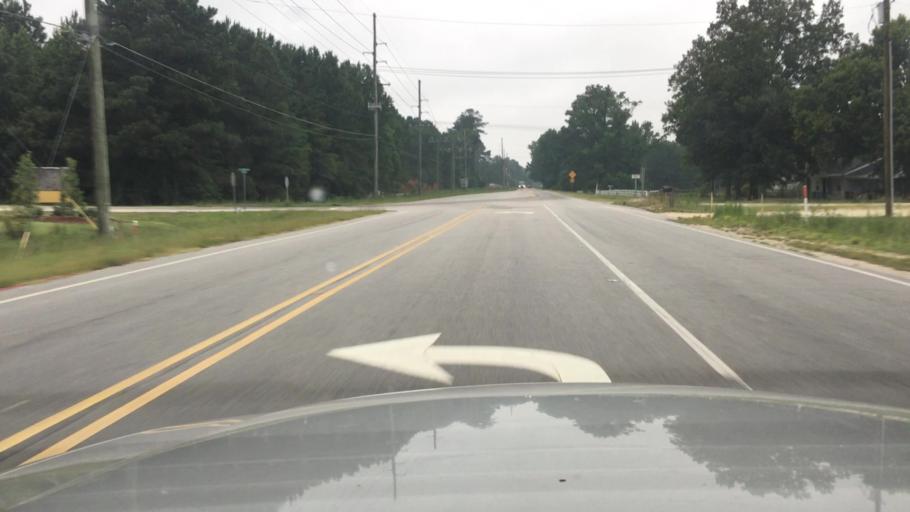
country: US
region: North Carolina
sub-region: Cumberland County
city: Fayetteville
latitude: 35.0099
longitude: -78.8636
